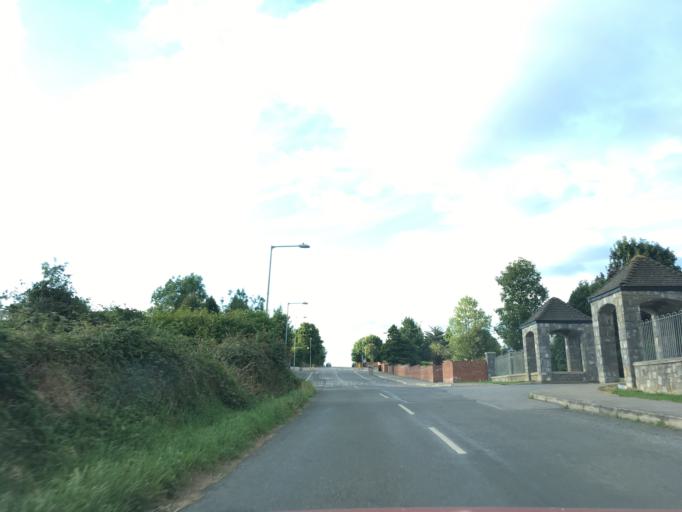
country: IE
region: Munster
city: Cashel
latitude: 52.5087
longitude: -7.8857
